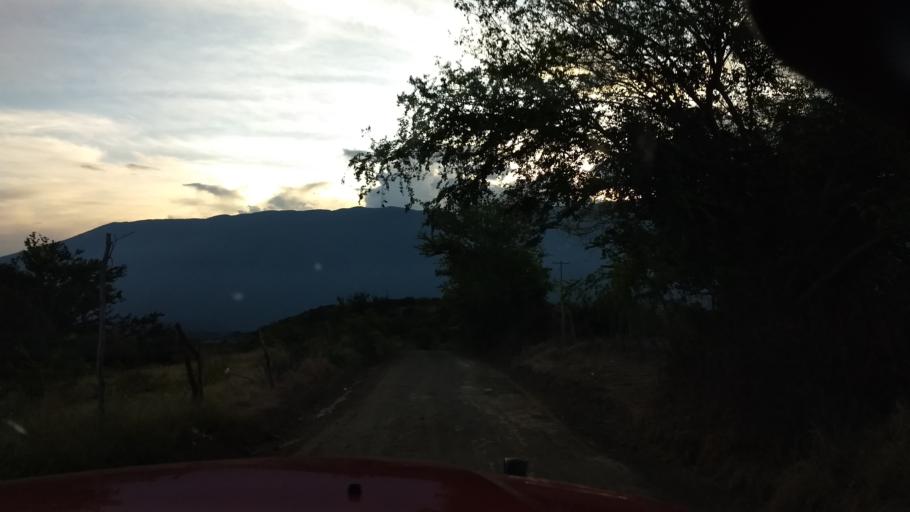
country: MX
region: Colima
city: Suchitlan
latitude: 19.4851
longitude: -103.7942
